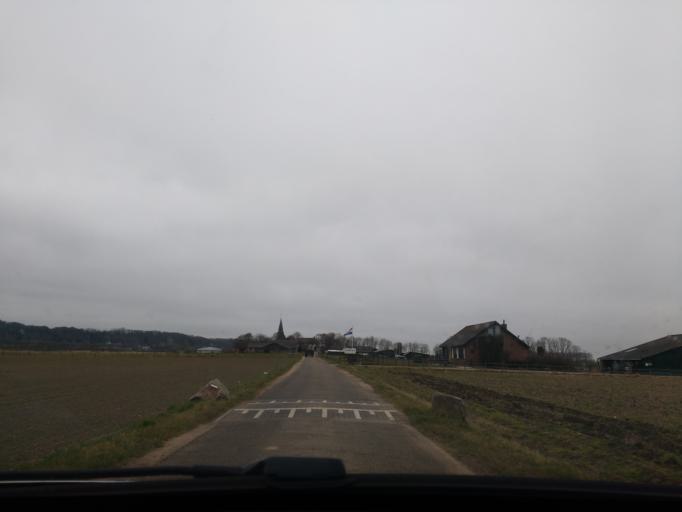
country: NL
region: Gelderland
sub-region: Gemeente Groesbeek
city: Berg en Dal
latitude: 51.8408
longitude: 5.9236
